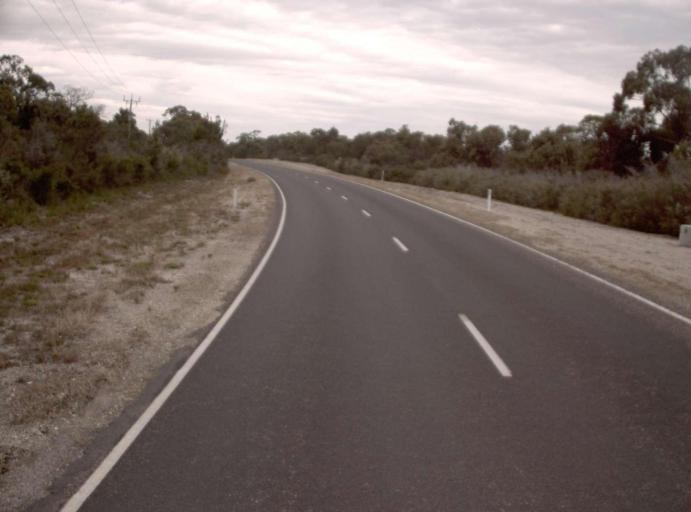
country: AU
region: Victoria
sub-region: Wellington
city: Sale
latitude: -38.1814
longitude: 147.3768
